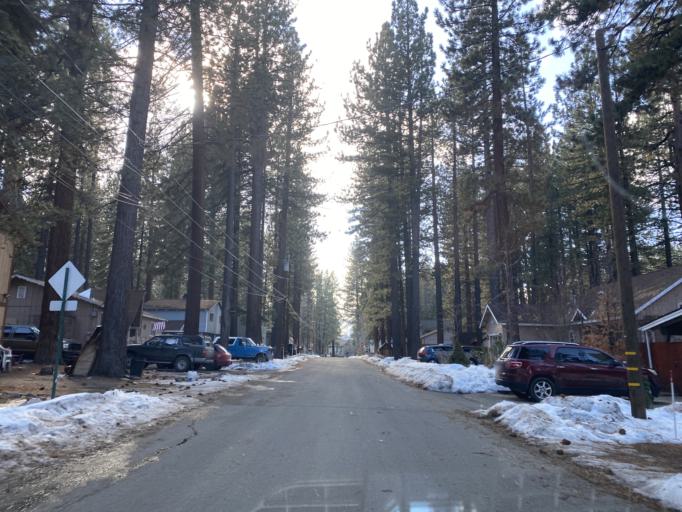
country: US
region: California
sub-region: El Dorado County
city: South Lake Tahoe
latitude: 38.9222
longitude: -119.9834
